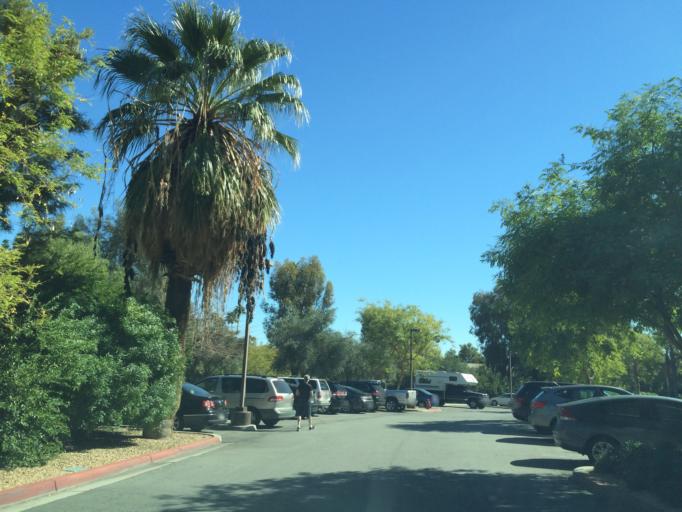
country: US
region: California
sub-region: Riverside County
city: Palm Springs
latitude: 33.8473
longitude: -116.5433
